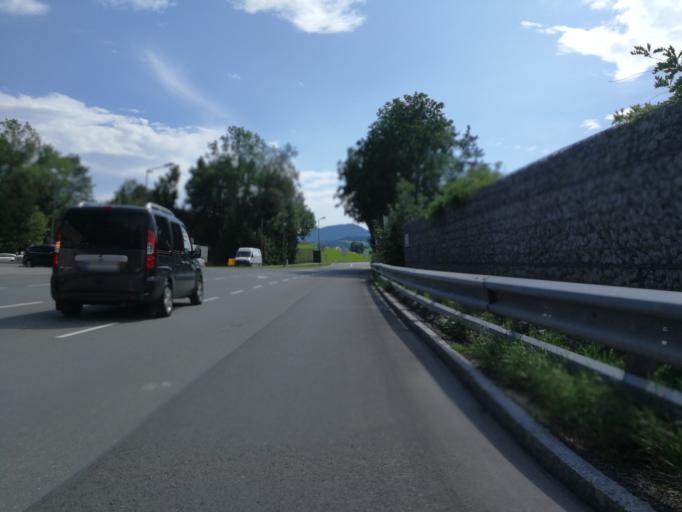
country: AT
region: Salzburg
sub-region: Politischer Bezirk Salzburg-Umgebung
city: Henndorf am Wallersee
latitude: 47.8926
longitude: 13.1805
